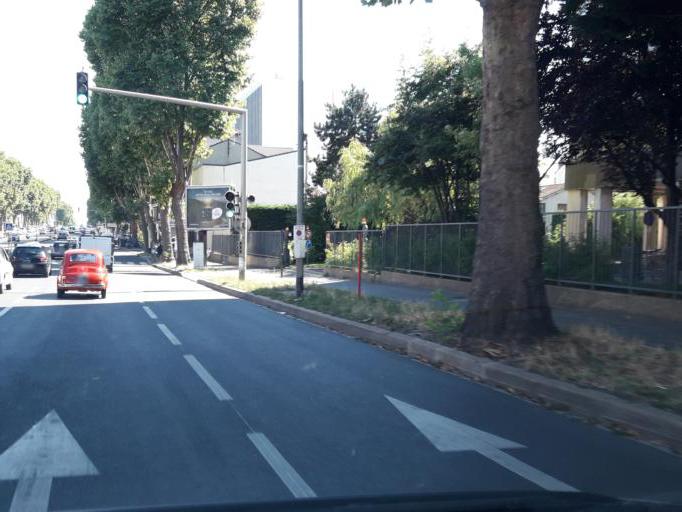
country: FR
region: Ile-de-France
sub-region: Departement du Val-de-Marne
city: Arcueil
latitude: 48.8003
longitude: 2.3233
